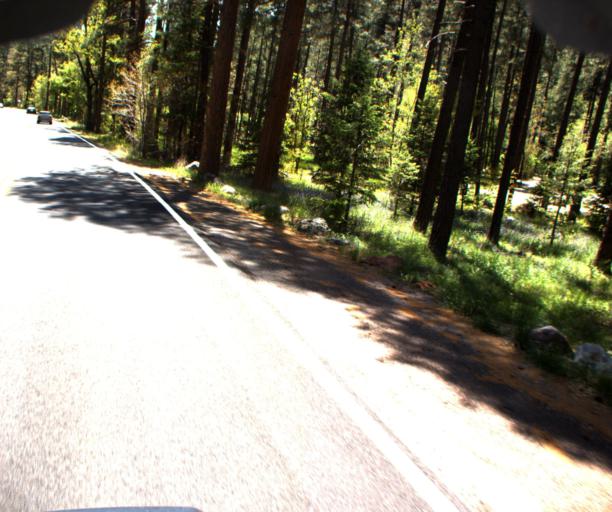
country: US
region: Arizona
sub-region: Coconino County
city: Kachina Village
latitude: 35.0117
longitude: -111.7381
